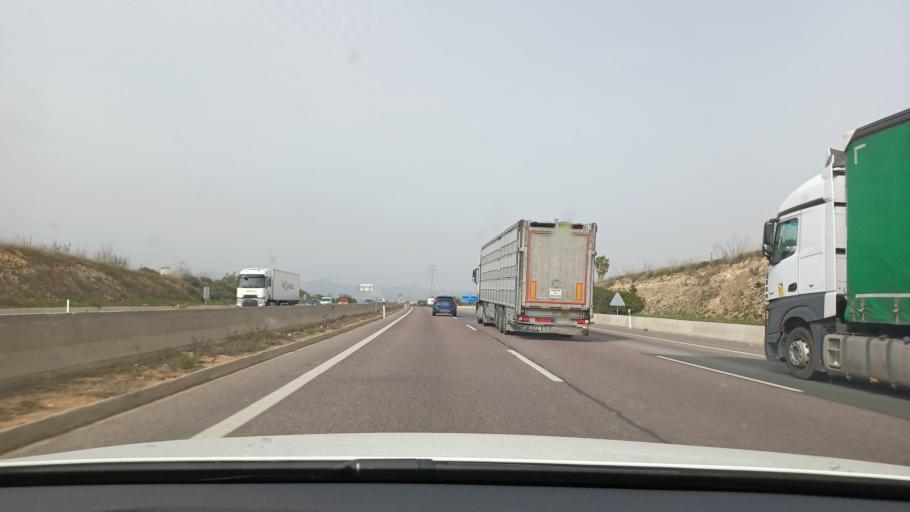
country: ES
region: Valencia
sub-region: Provincia de Valencia
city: Betera
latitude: 39.5630
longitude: -0.4273
